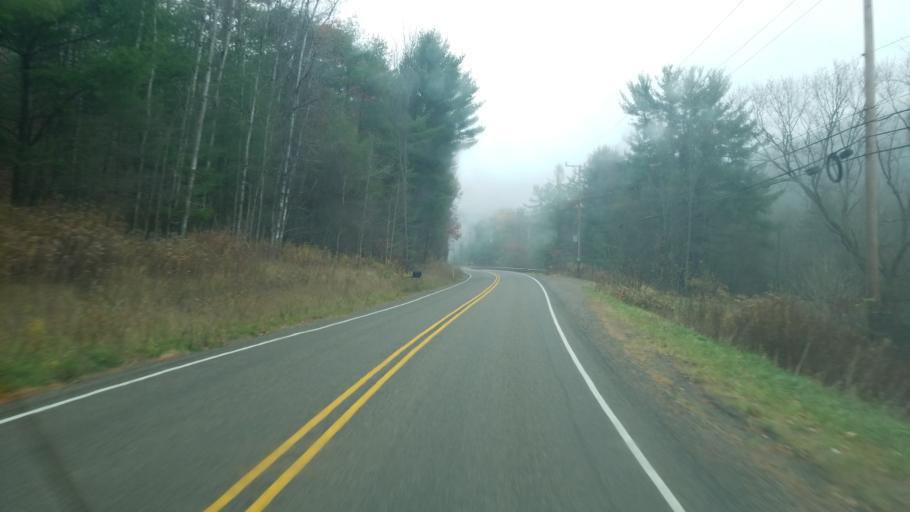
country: US
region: Pennsylvania
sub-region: McKean County
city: Smethport
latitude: 41.8990
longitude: -78.5214
